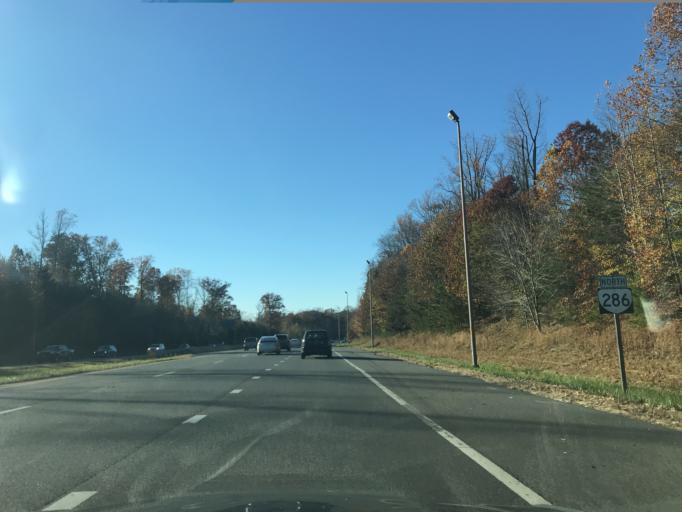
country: US
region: Virginia
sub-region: Fairfax County
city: Greenbriar
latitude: 38.8476
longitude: -77.3803
